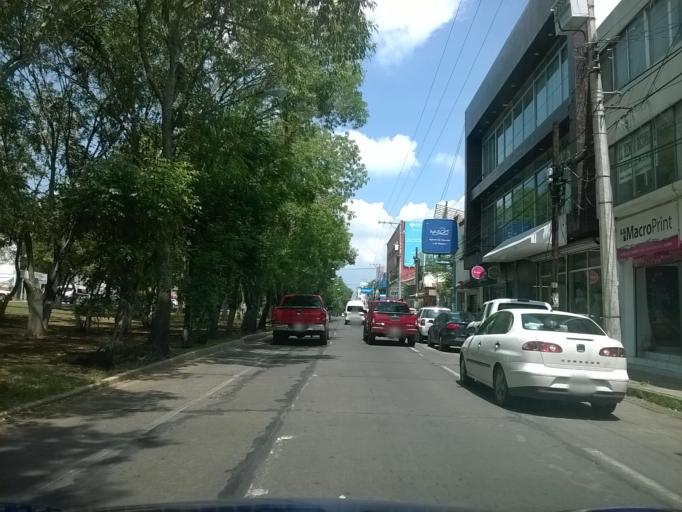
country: MX
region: Michoacan
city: Morelia
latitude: 19.6887
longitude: -101.1646
